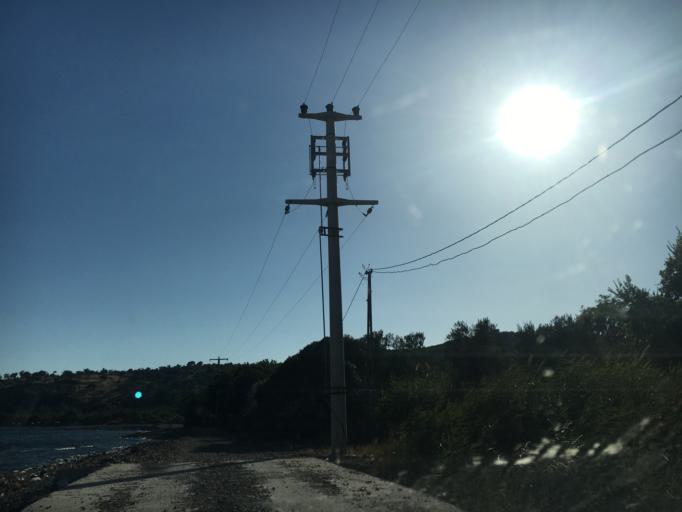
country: TR
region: Canakkale
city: Behram
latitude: 39.4804
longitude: 26.2570
